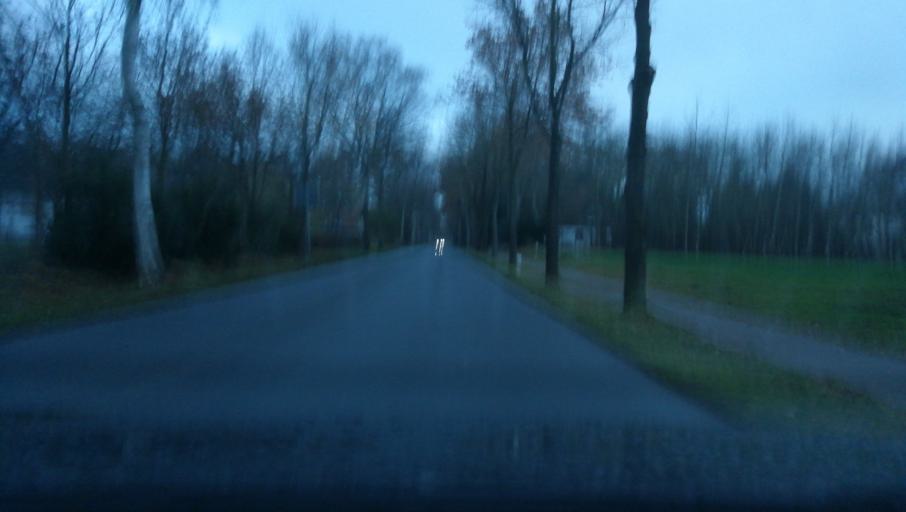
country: DE
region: Lower Saxony
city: Fintel
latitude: 53.1624
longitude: 9.6641
